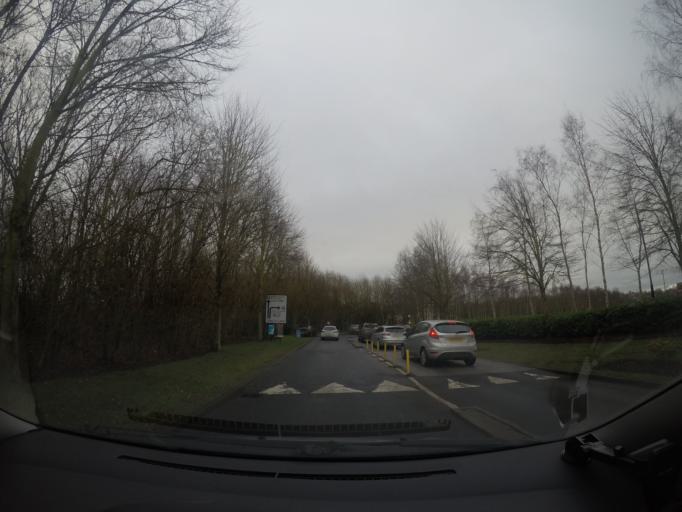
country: GB
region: England
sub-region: City of York
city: Fulford
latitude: 53.9221
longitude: -1.0732
